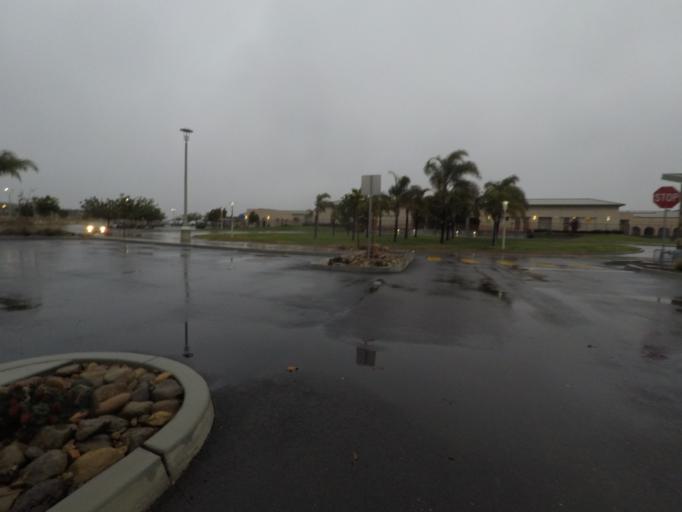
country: MX
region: Baja California
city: Tijuana
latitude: 32.5705
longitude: -117.0240
